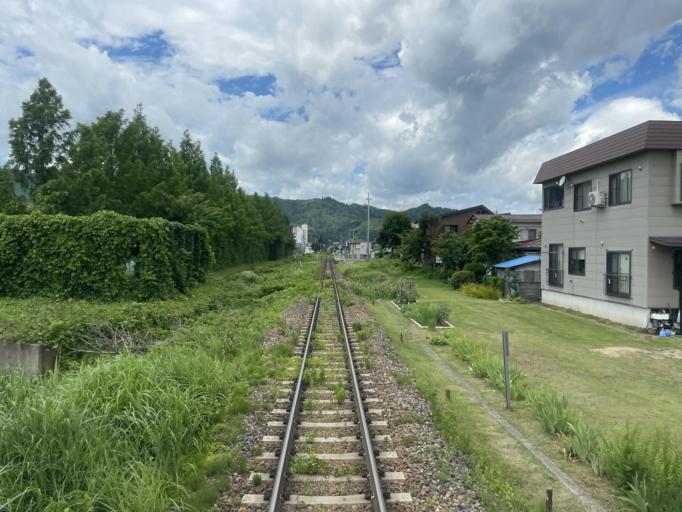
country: JP
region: Yamagata
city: Yonezawa
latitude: 37.8961
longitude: 140.1097
